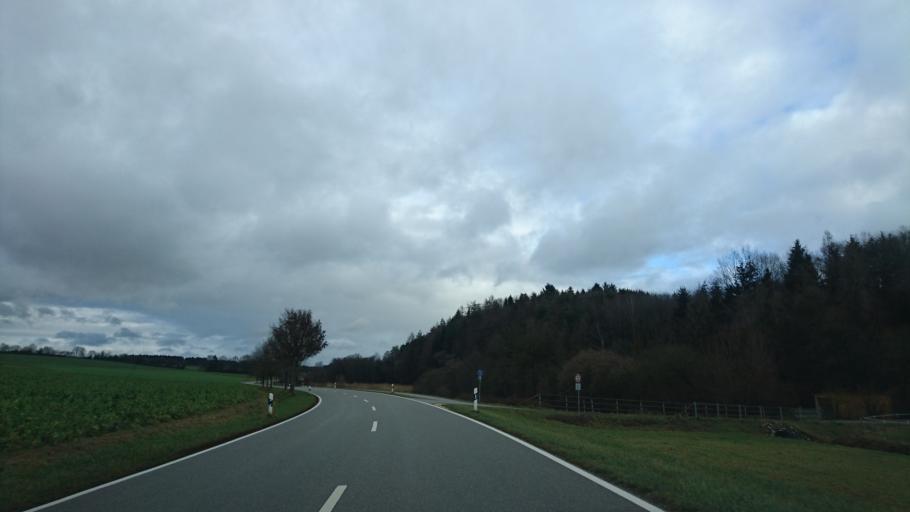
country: DE
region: Bavaria
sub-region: Swabia
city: Heretsried
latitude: 48.4759
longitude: 10.7219
